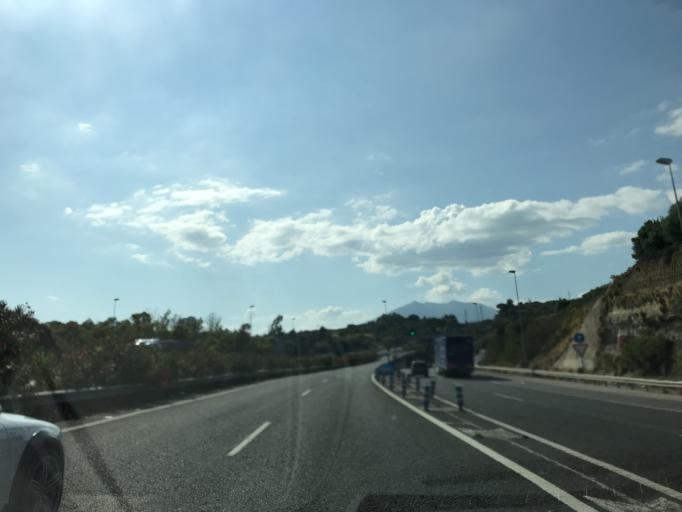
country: ES
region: Andalusia
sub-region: Provincia de Malaga
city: Marbella
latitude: 36.5132
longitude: -4.9308
